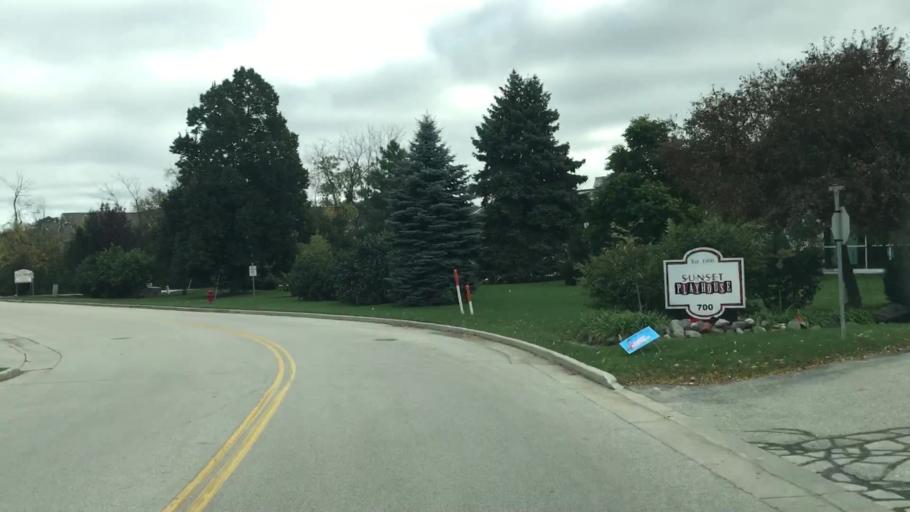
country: US
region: Wisconsin
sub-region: Waukesha County
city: Elm Grove
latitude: 43.0403
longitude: -88.0785
